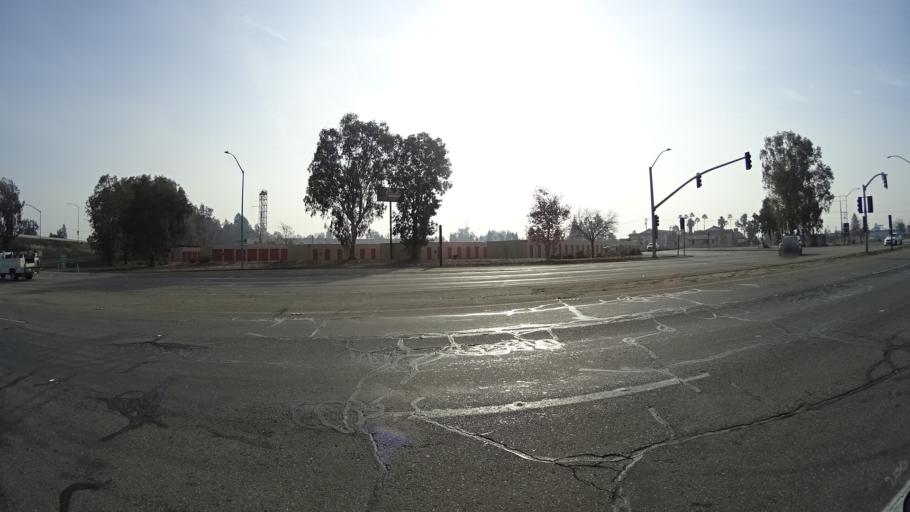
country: US
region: California
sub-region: Kern County
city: Oildale
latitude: 35.4016
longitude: -119.0423
